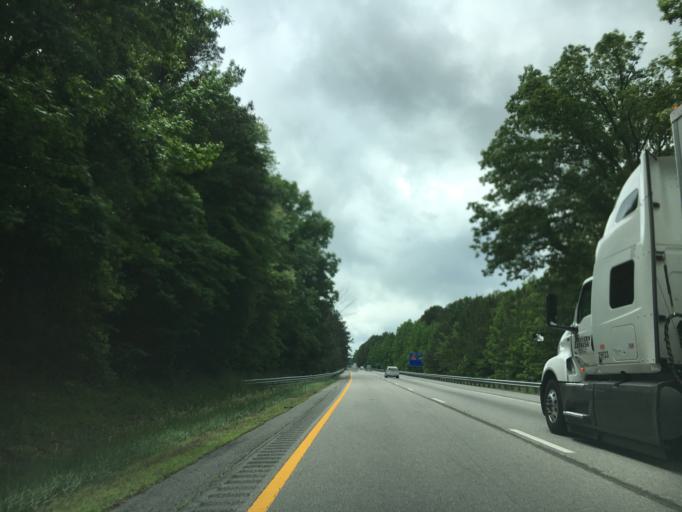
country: US
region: Virginia
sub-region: Mecklenburg County
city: South Hill
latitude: 36.7669
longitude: -78.0675
